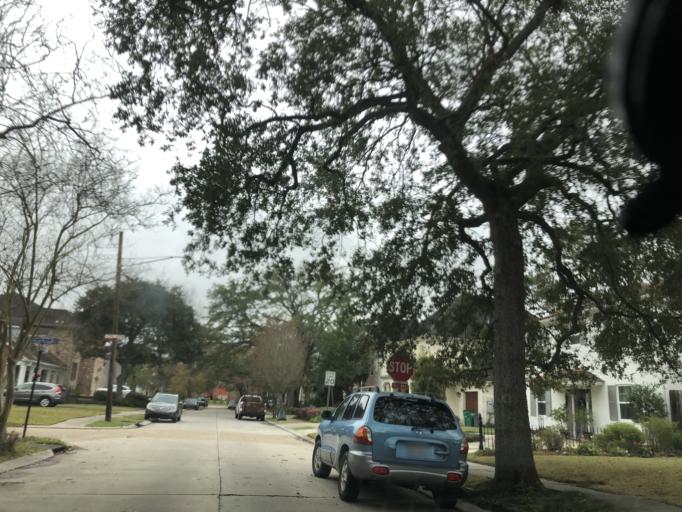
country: US
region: Louisiana
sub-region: Jefferson Parish
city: Metairie
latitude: 29.9790
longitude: -90.1502
